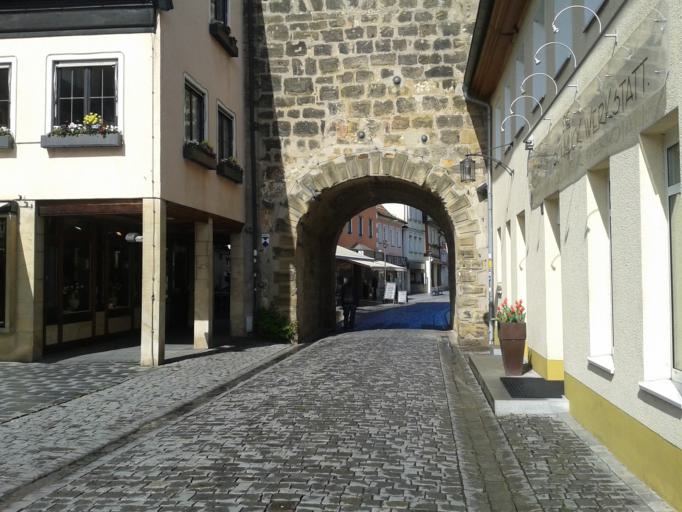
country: DE
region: Bavaria
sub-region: Upper Franconia
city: Lichtenfels
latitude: 50.1452
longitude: 11.0615
